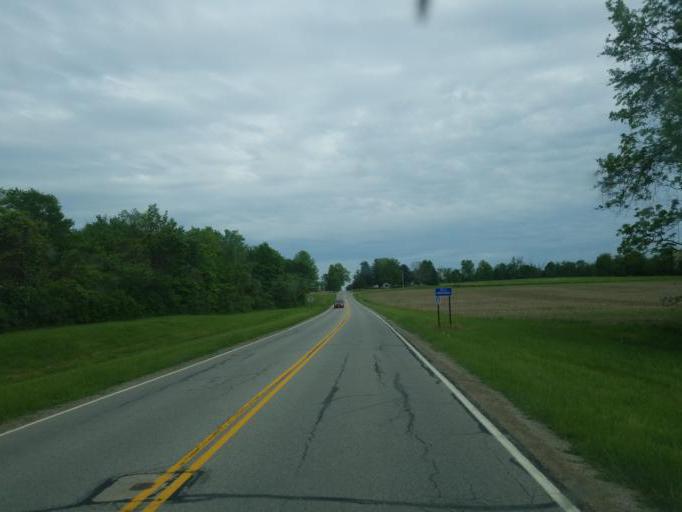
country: US
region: Ohio
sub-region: Richland County
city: Ontario
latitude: 40.7823
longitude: -82.6294
